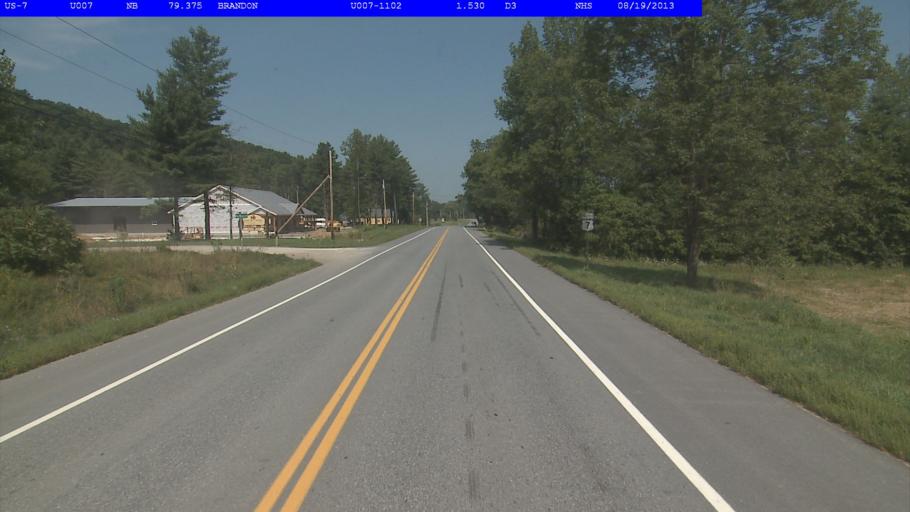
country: US
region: Vermont
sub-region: Rutland County
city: Brandon
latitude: 43.7758
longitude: -73.0546
